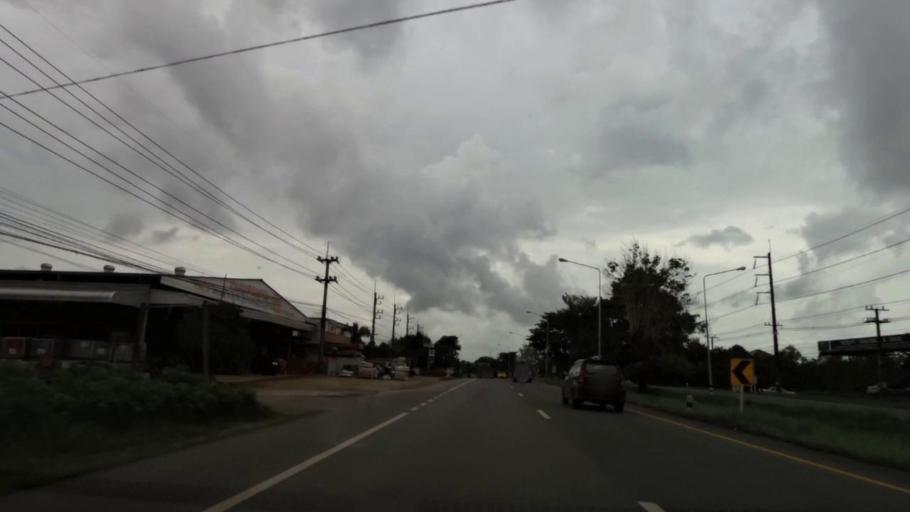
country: TH
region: Chanthaburi
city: Tha Mai
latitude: 12.6932
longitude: 101.9932
